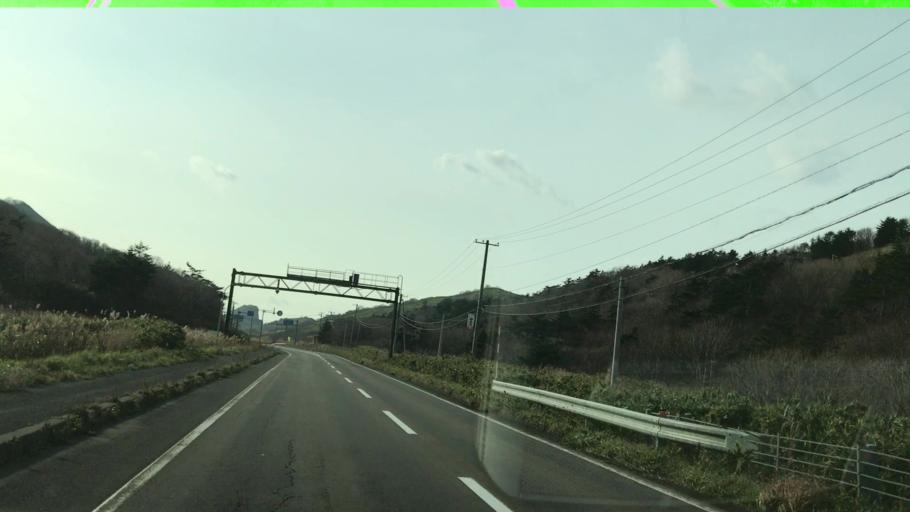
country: JP
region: Hokkaido
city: Iwanai
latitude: 43.3262
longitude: 140.3645
